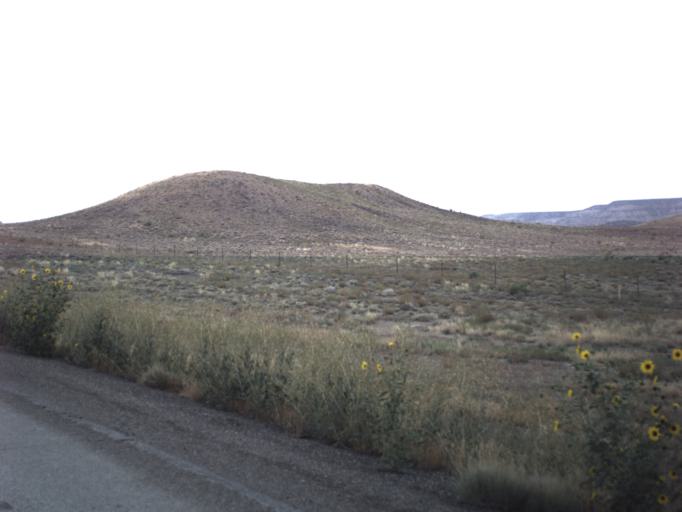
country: US
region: Utah
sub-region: Carbon County
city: East Carbon City
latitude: 39.4577
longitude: -110.4836
